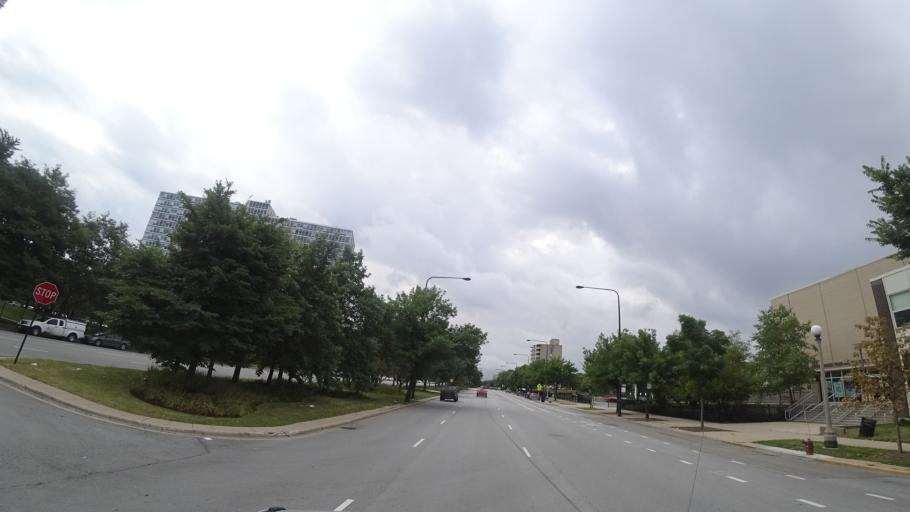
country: US
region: Illinois
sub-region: Cook County
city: Chicago
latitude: 41.8404
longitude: -87.6175
